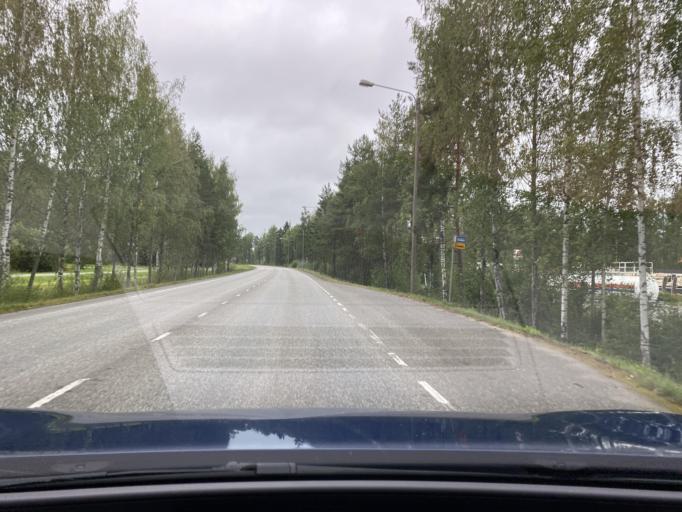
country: FI
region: Kymenlaakso
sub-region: Kouvola
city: Kouvola
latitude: 60.8990
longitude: 26.6057
